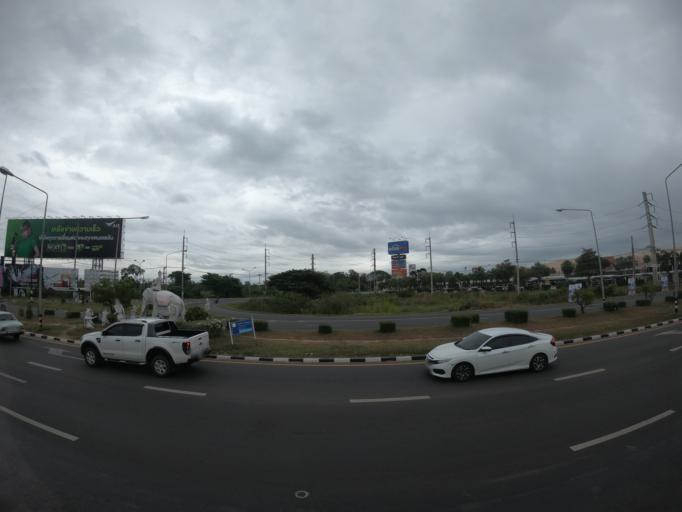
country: TH
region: Roi Et
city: Roi Et
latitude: 16.0630
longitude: 103.6189
